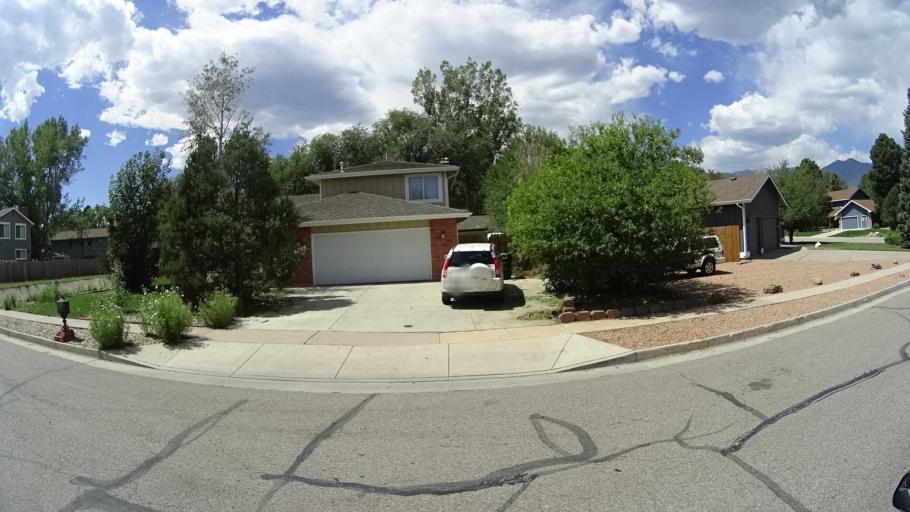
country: US
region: Colorado
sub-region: El Paso County
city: Stratmoor
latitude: 38.7747
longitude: -104.8169
